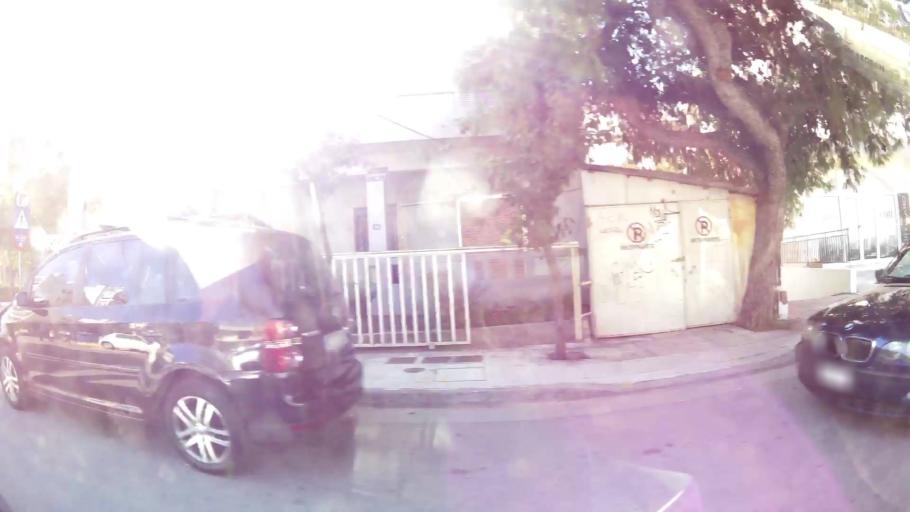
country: GR
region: Attica
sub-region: Nomarchia Athinas
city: Metamorfosi
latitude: 38.0636
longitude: 23.7569
